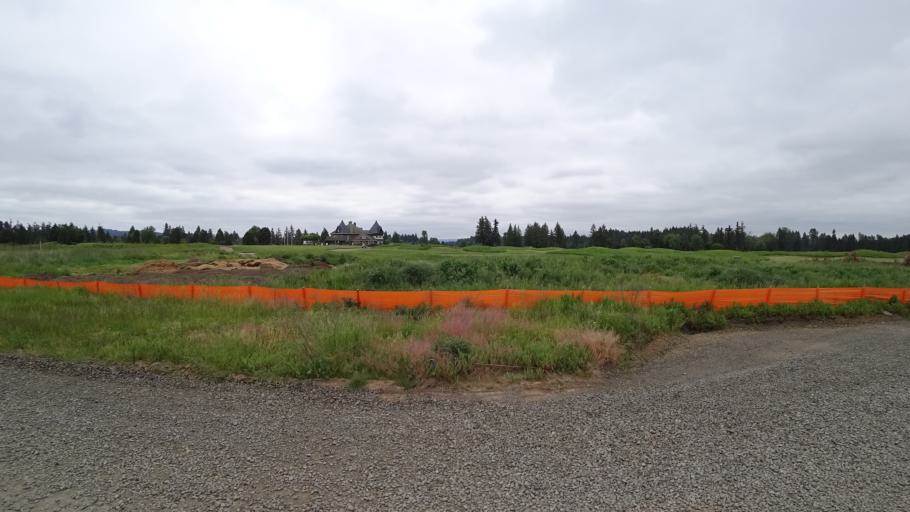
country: US
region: Oregon
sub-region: Washington County
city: Aloha
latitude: 45.4873
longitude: -122.9188
